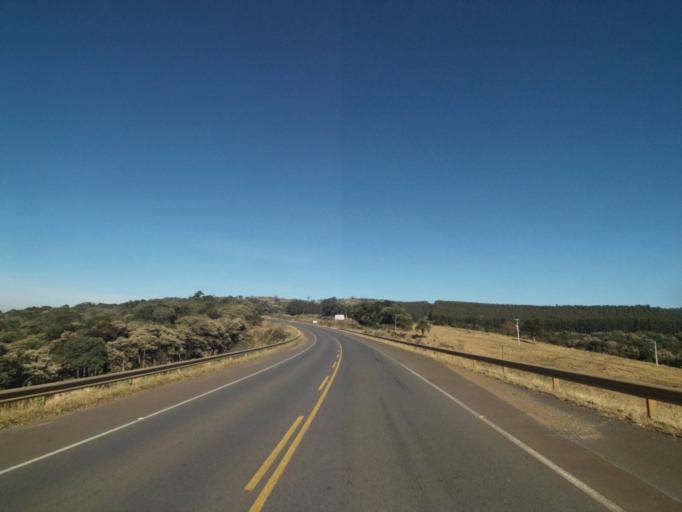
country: BR
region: Parana
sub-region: Tibagi
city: Tibagi
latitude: -24.4017
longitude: -50.3414
